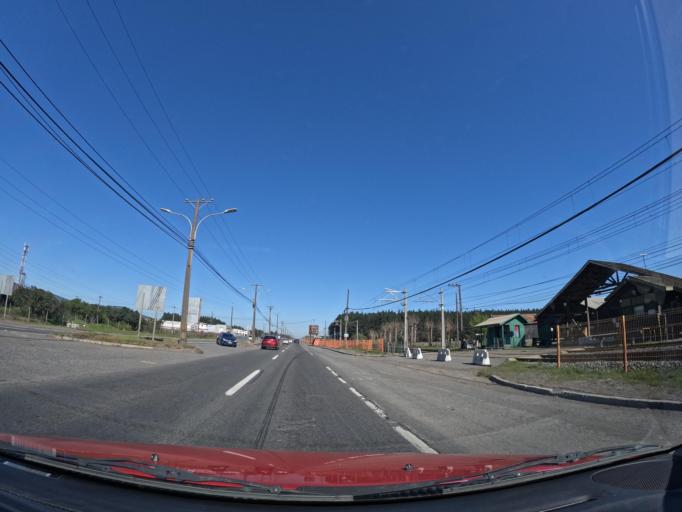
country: CL
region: Biobio
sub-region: Provincia de Concepcion
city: Chiguayante
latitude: -36.9062
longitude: -73.1451
